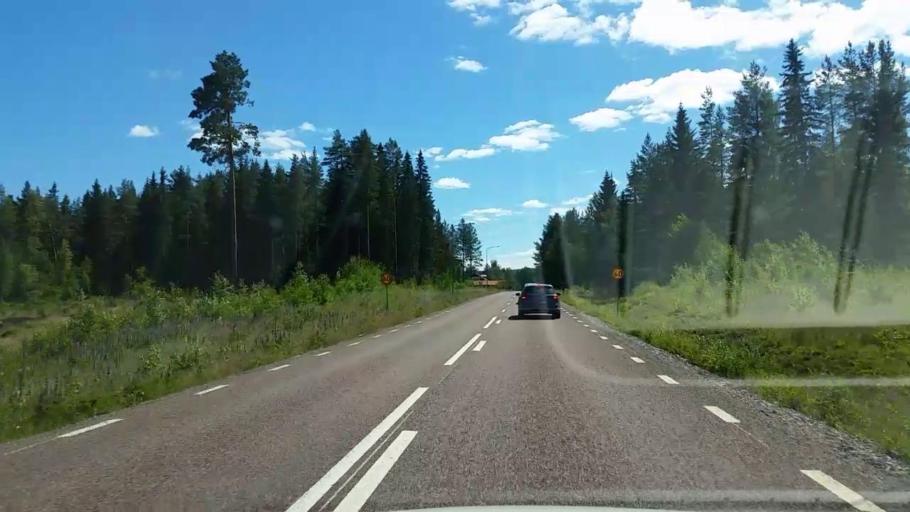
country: SE
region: Gaevleborg
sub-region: Ovanakers Kommun
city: Edsbyn
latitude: 61.2086
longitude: 15.8709
